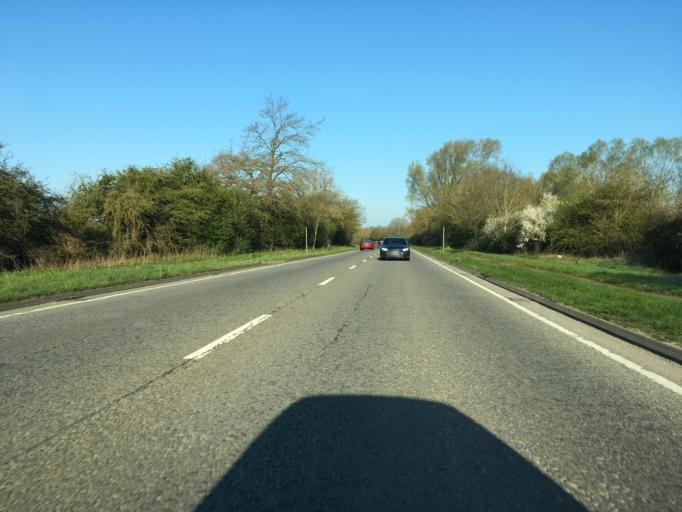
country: GB
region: England
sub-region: Oxfordshire
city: Yarnton
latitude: 51.7924
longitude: -1.3012
